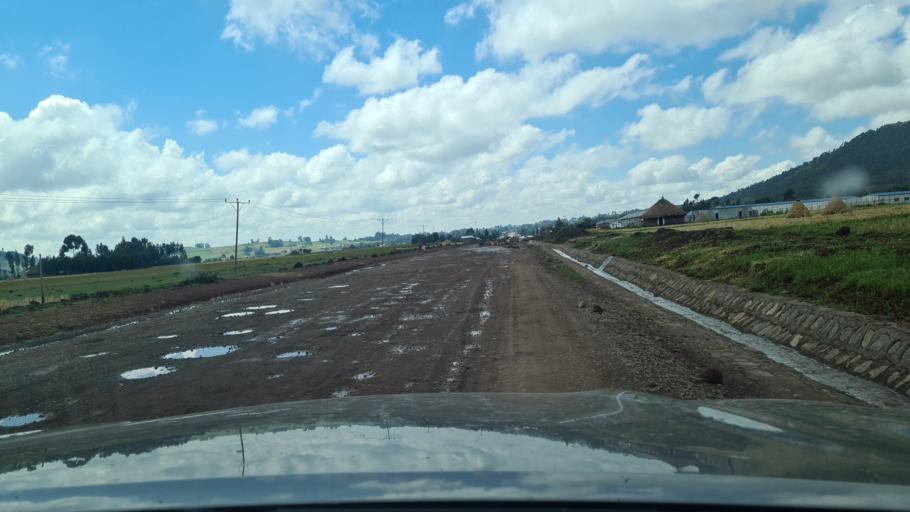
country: ET
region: Oromiya
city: Huruta
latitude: 8.0833
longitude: 39.5426
